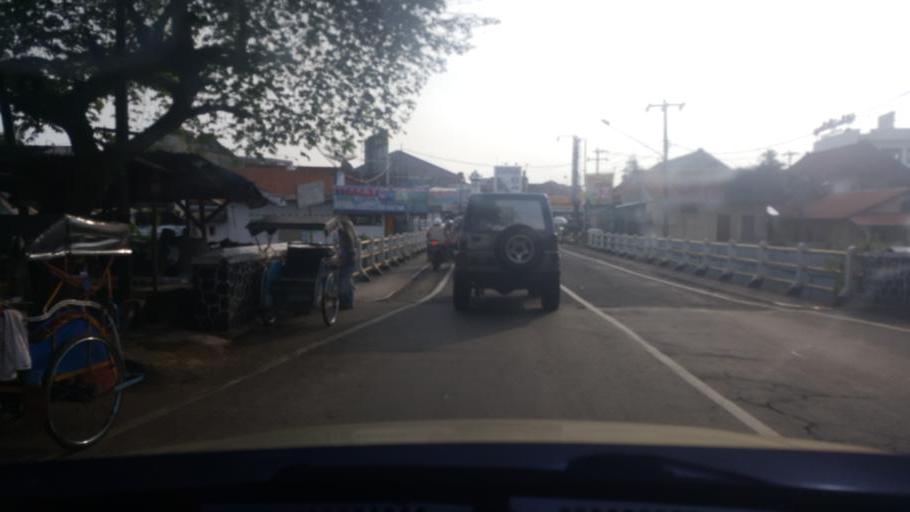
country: ID
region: West Java
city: Tawangsari
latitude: -7.3195
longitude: 108.2205
